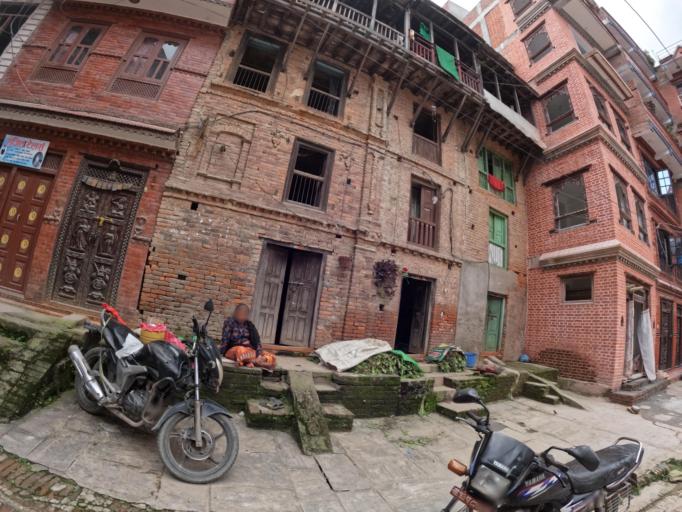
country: NP
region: Central Region
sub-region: Bagmati Zone
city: Bhaktapur
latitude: 27.6848
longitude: 85.3846
